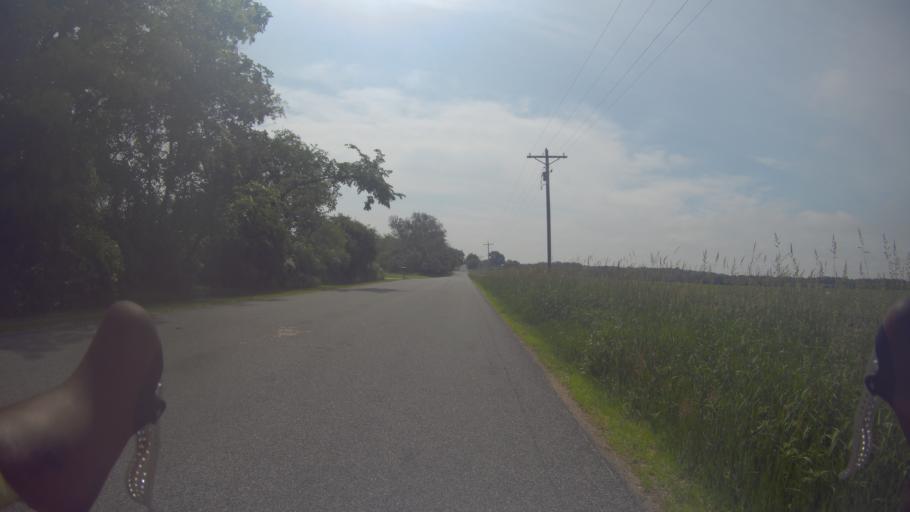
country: US
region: Wisconsin
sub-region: Rock County
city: Edgerton
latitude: 42.8571
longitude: -89.0426
